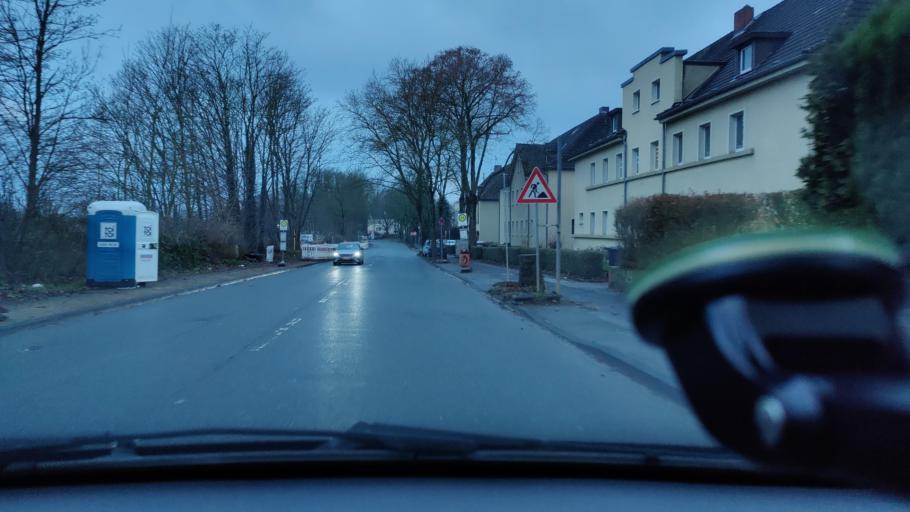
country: DE
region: North Rhine-Westphalia
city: Castrop-Rauxel
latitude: 51.4878
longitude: 7.2938
